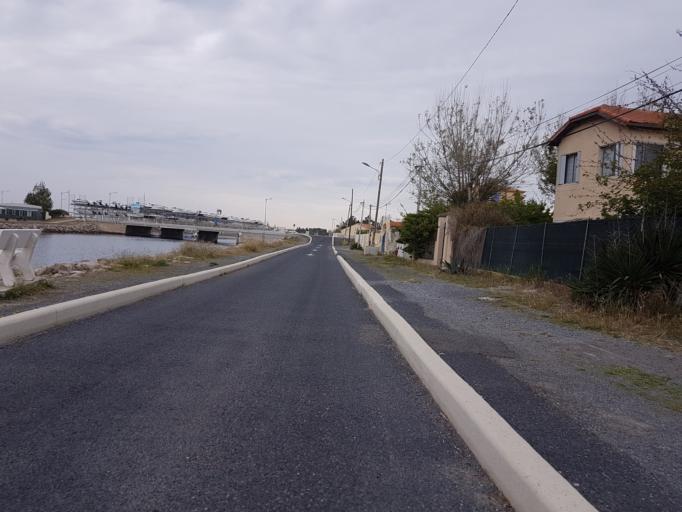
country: FR
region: Languedoc-Roussillon
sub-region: Departement de l'Herault
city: Marseillan
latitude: 43.3206
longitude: 3.5537
